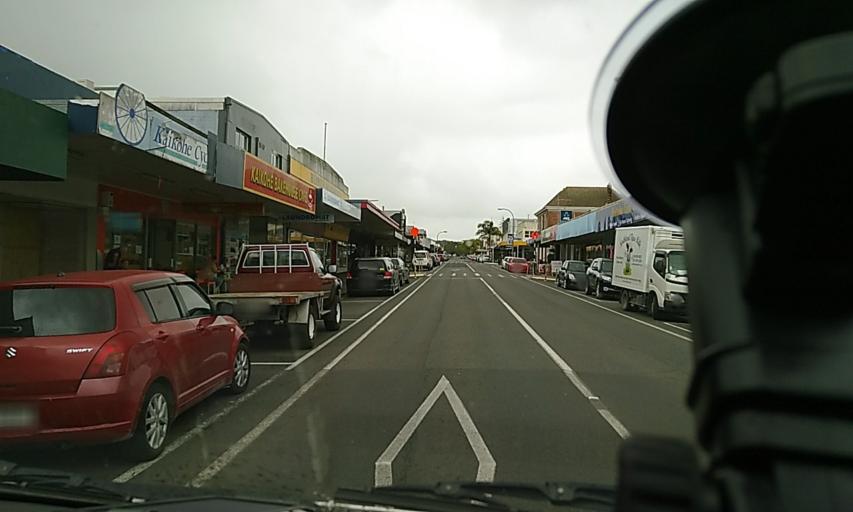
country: NZ
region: Northland
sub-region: Far North District
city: Waimate North
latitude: -35.4071
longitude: 173.8008
